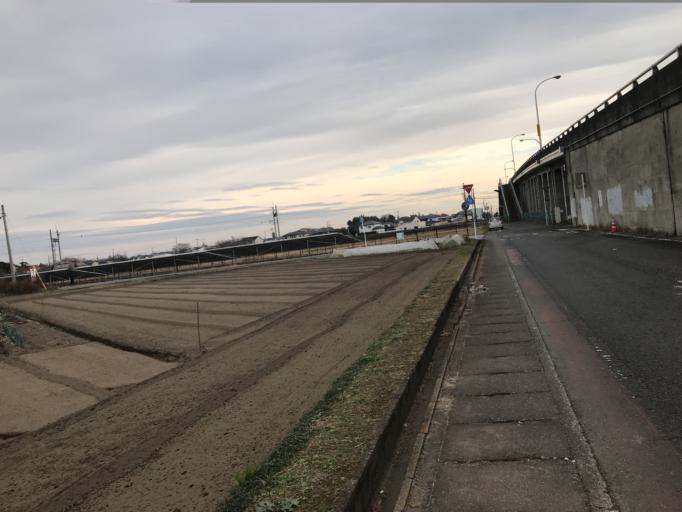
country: JP
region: Gunma
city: Ota
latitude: 36.3059
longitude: 139.3968
